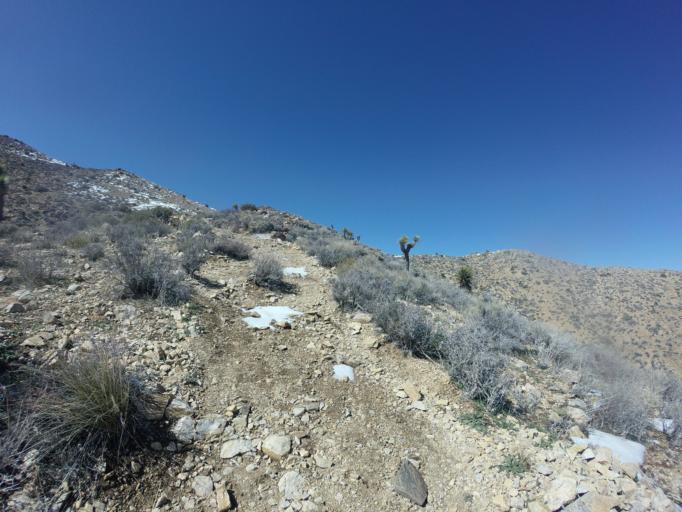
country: US
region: California
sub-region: San Bernardino County
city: Twentynine Palms
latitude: 33.9379
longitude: -116.1341
